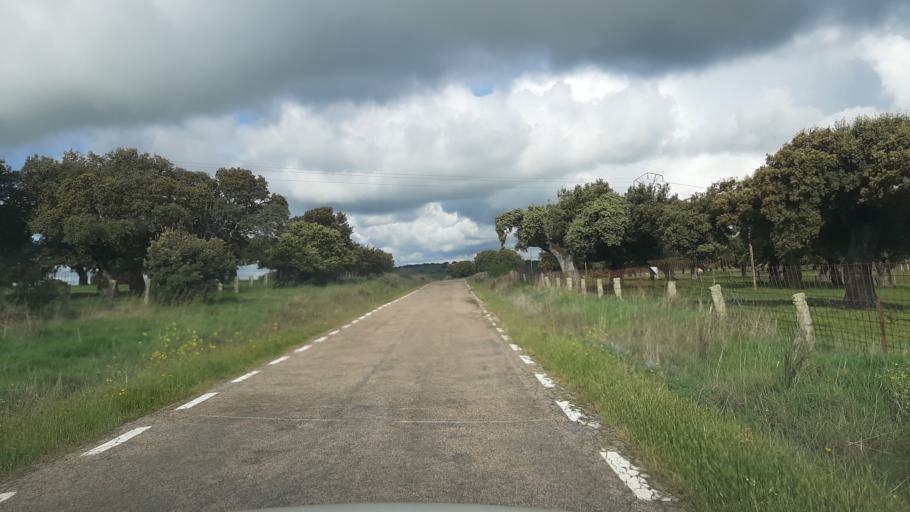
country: ES
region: Castille and Leon
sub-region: Provincia de Salamanca
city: Narros de Matalayegua
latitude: 40.7032
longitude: -5.9129
